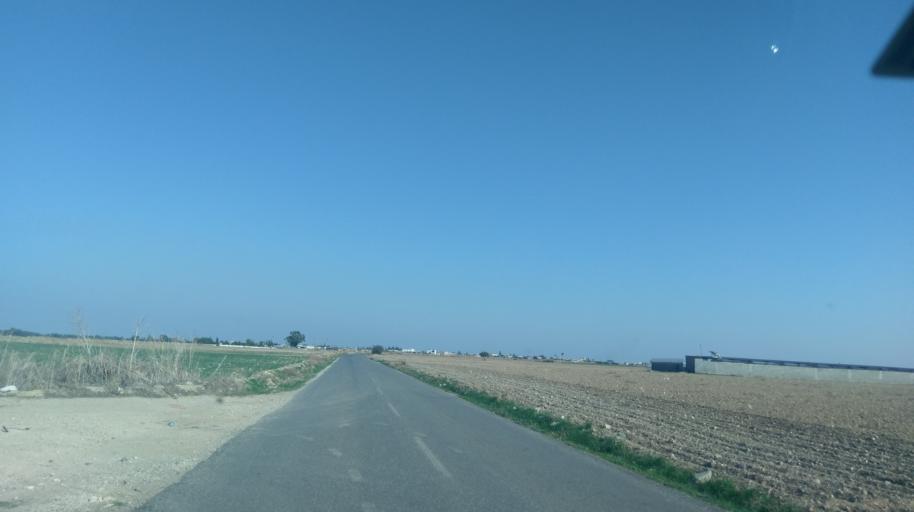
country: CY
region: Larnaka
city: Pergamos
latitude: 35.1023
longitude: 33.6610
